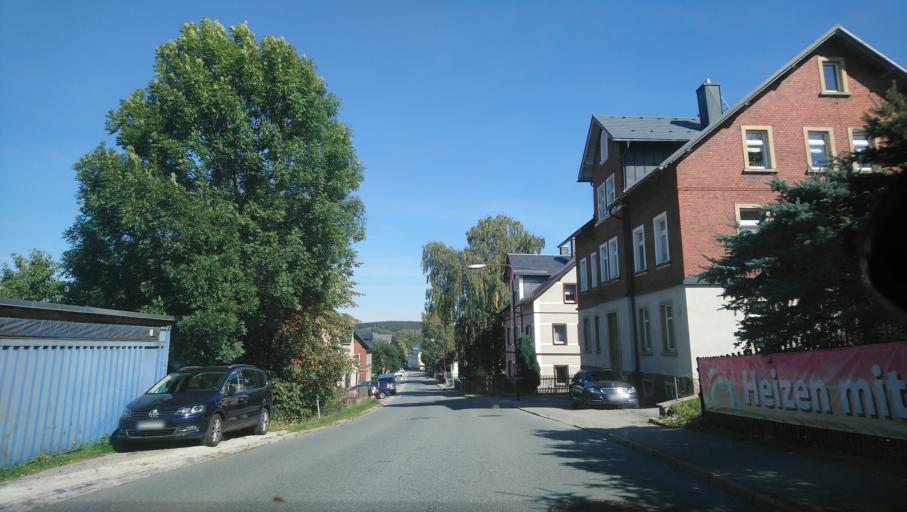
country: DE
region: Saxony
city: Crottendorf
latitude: 50.5116
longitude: 12.9898
